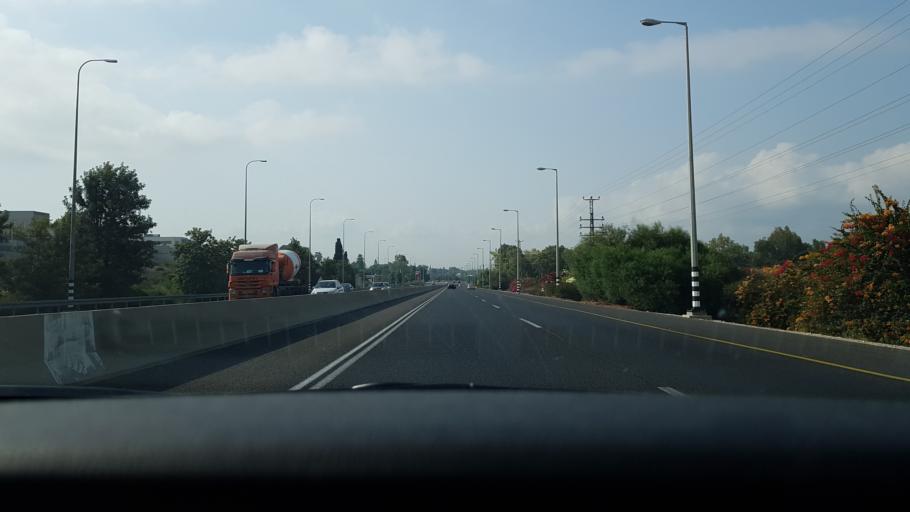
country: IL
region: Central District
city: Ness Ziona
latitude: 31.9281
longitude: 34.7732
